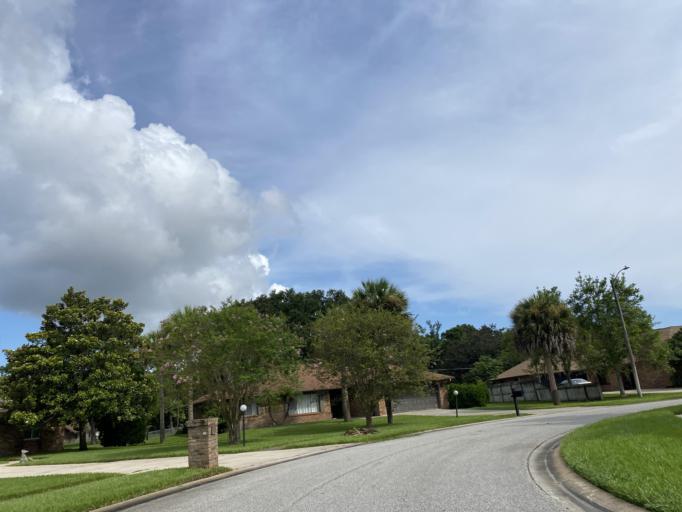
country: US
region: Florida
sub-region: Volusia County
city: Port Orange
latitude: 29.1366
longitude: -81.0022
